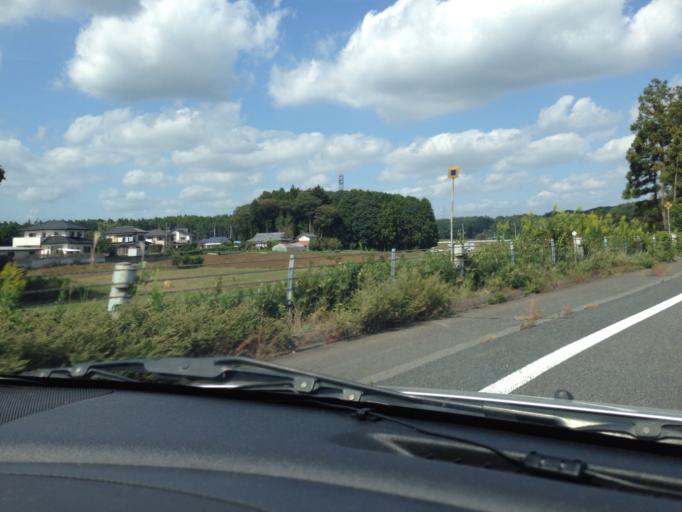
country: JP
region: Ibaraki
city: Mito-shi
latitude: 36.3940
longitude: 140.3880
